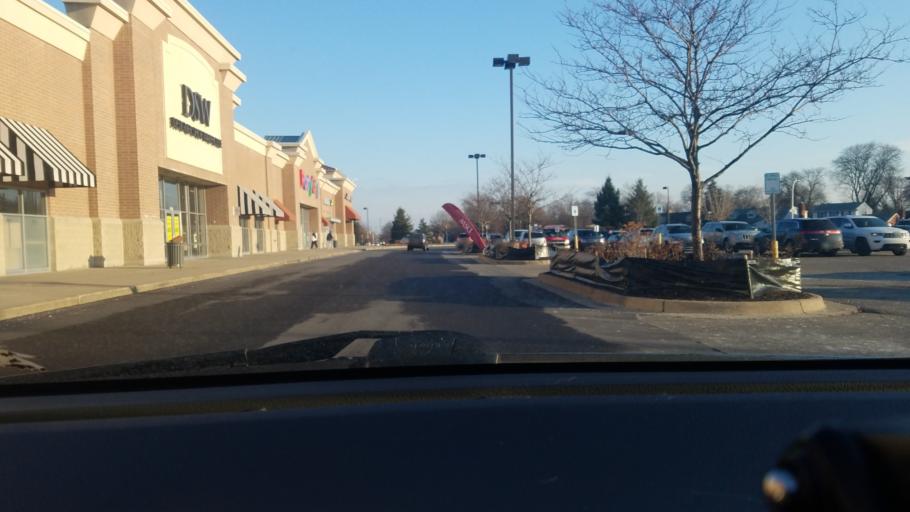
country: US
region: Michigan
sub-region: Wayne County
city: Allen Park
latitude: 42.2791
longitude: -83.2112
